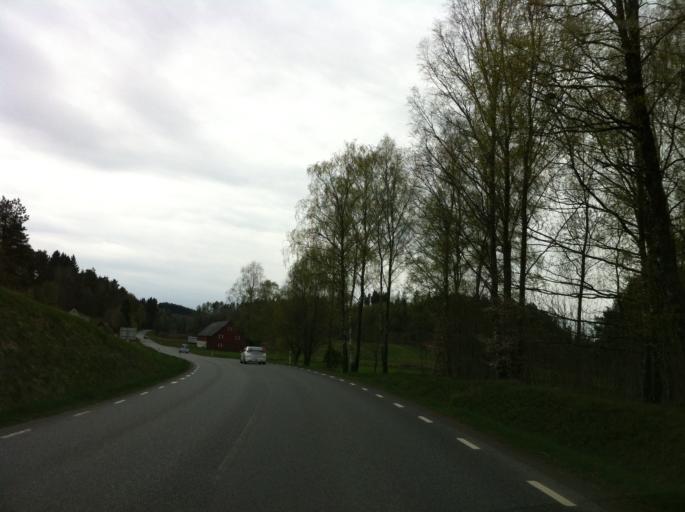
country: SE
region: Halland
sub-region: Halmstads Kommun
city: Getinge
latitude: 57.1256
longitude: 12.7115
